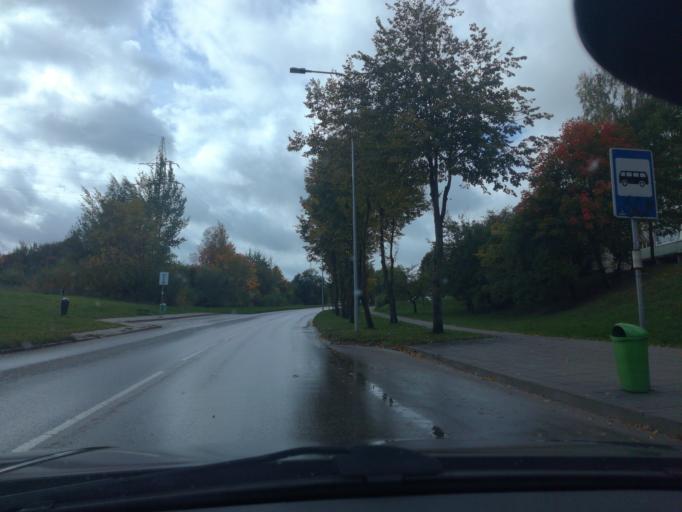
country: LT
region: Alytaus apskritis
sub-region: Alytus
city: Alytus
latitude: 54.3902
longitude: 24.0289
